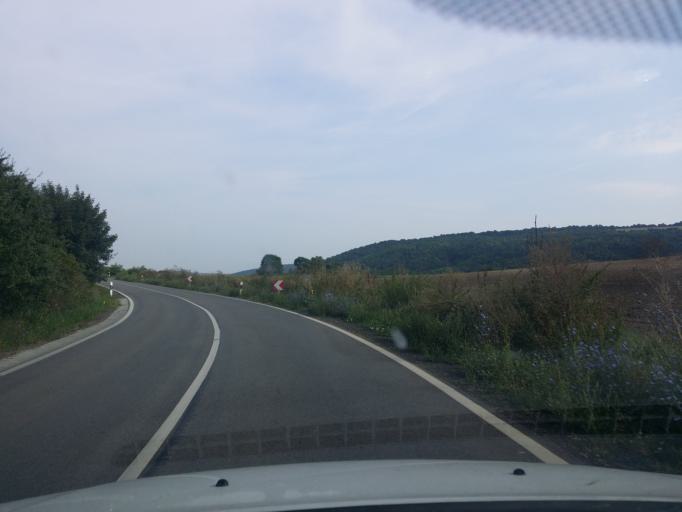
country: HU
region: Pest
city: Acsa
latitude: 47.7574
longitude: 19.3685
